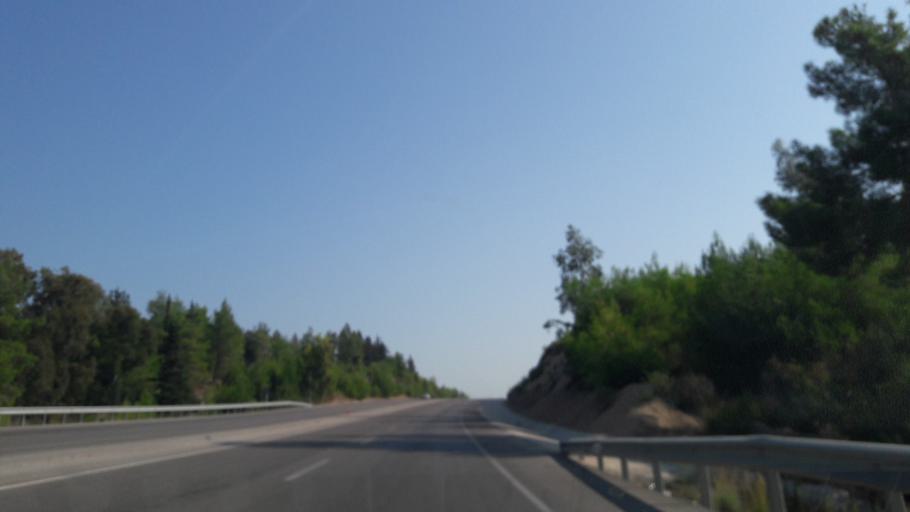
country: TR
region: Adana
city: Sagkaya
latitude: 37.1523
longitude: 35.5451
